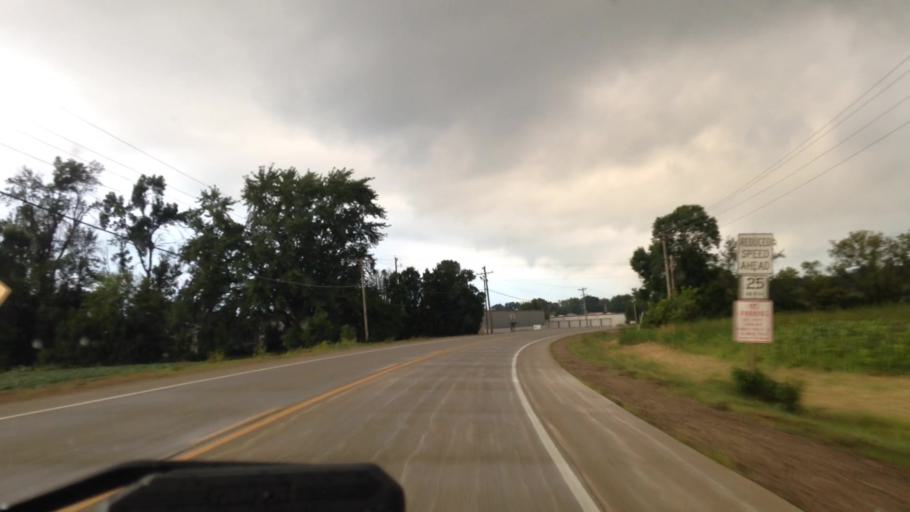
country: US
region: Wisconsin
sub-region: Dodge County
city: Mayville
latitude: 43.4821
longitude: -88.5535
